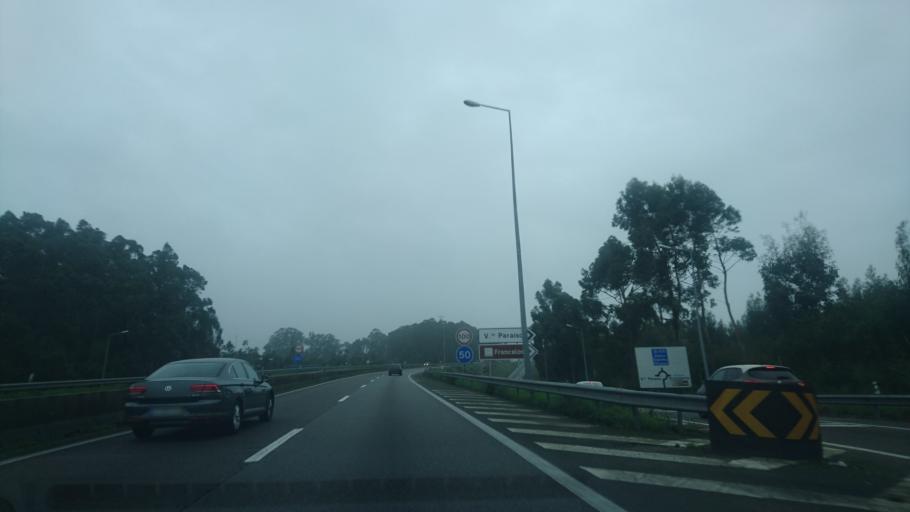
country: PT
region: Porto
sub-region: Vila Nova de Gaia
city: Gulpilhares
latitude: 41.0885
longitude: -8.6308
